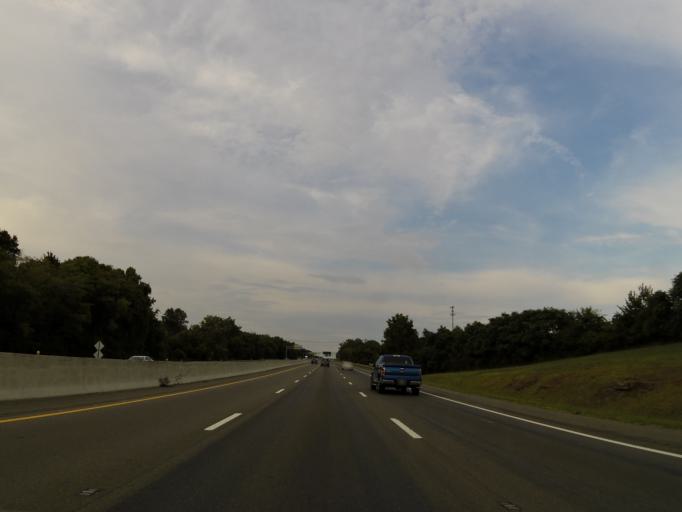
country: US
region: Tennessee
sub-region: Davidson County
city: Belle Meade
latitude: 36.1400
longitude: -86.8866
